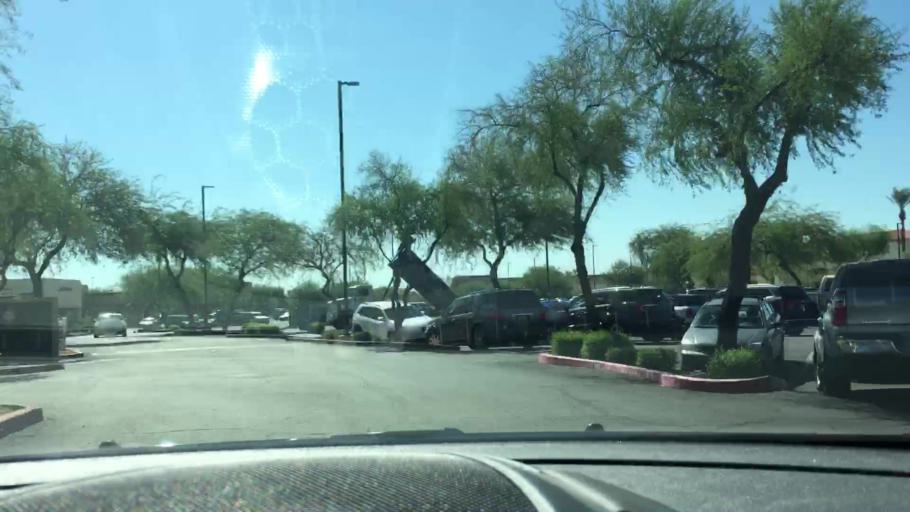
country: US
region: Arizona
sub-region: Maricopa County
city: Paradise Valley
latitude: 33.6276
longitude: -111.8920
